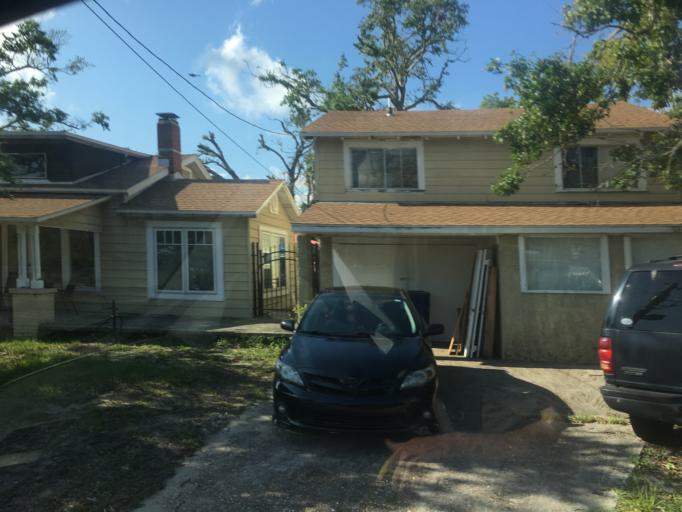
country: US
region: Florida
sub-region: Bay County
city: Springfield
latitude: 30.1532
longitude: -85.6264
